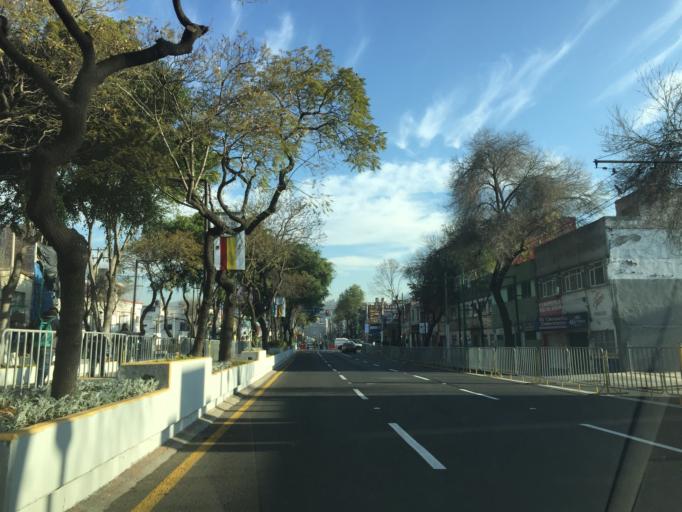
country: MX
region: Mexico
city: Colonia Lindavista
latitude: 19.4772
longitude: -99.1200
